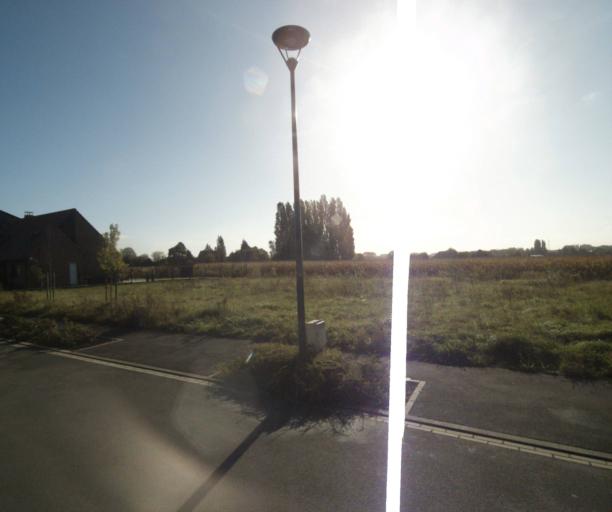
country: FR
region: Nord-Pas-de-Calais
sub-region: Departement du Nord
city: Verlinghem
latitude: 50.6784
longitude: 3.0006
